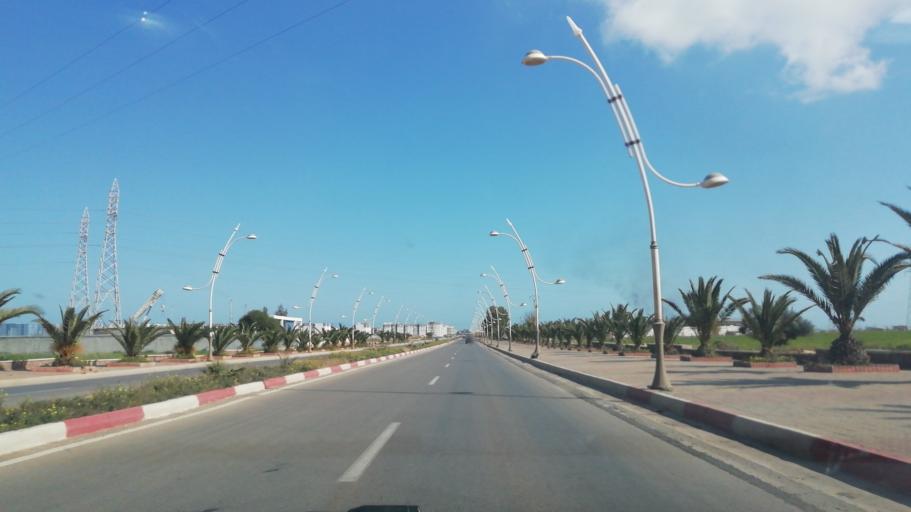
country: DZ
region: Oran
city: Ain el Bya
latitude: 35.7922
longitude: -0.2791
